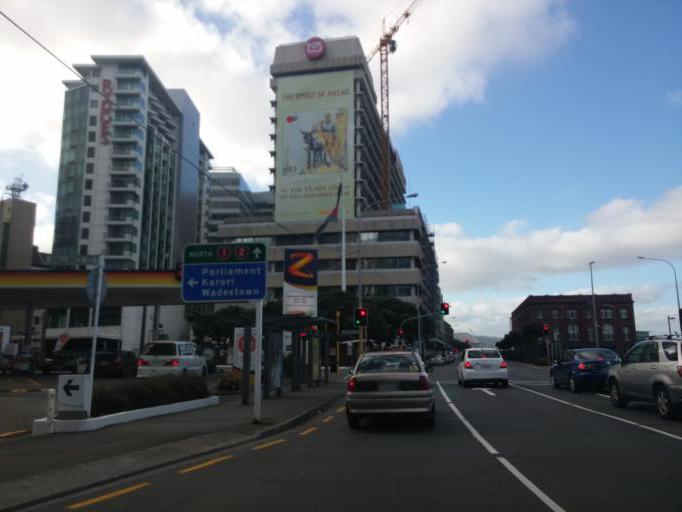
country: NZ
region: Wellington
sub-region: Wellington City
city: Wellington
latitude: -41.2821
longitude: 174.7786
